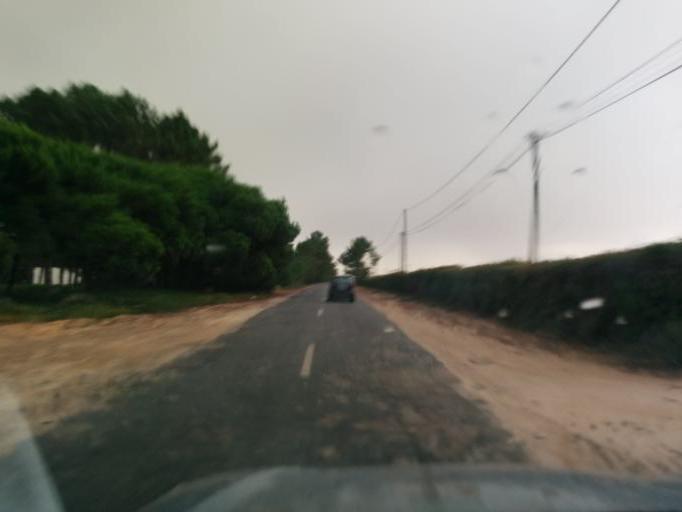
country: PT
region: Beja
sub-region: Odemira
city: Vila Nova de Milfontes
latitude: 37.6069
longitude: -8.7983
